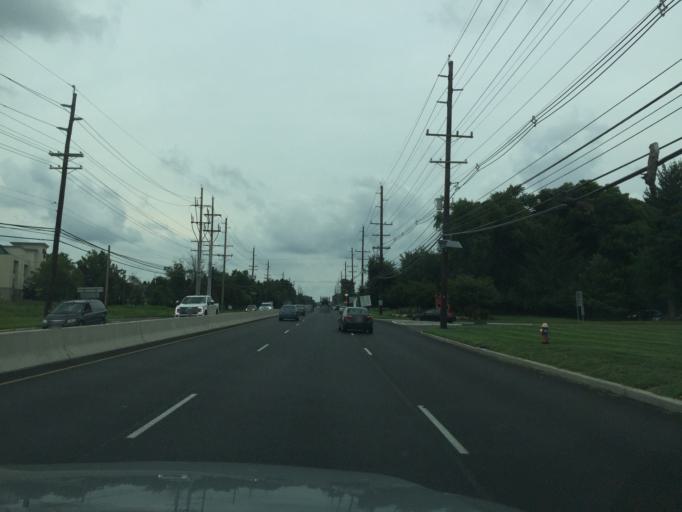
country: US
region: New Jersey
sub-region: Somerset County
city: Kingston
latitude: 40.3622
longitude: -74.6008
